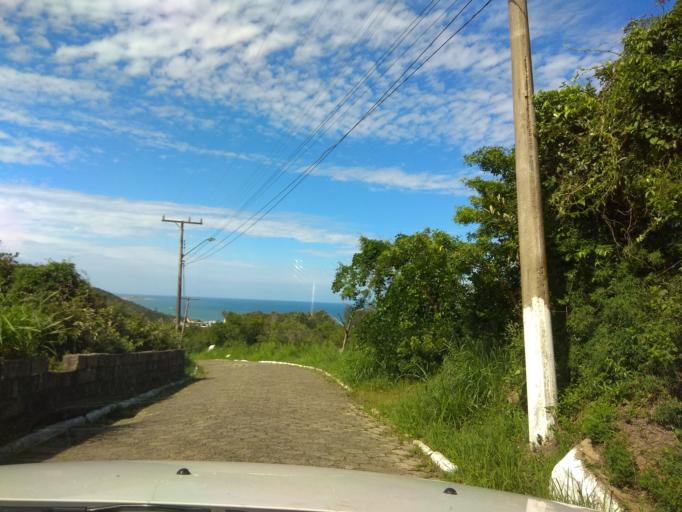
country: BR
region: Santa Catarina
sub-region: Laguna
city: Laguna
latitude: -28.4870
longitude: -48.7780
